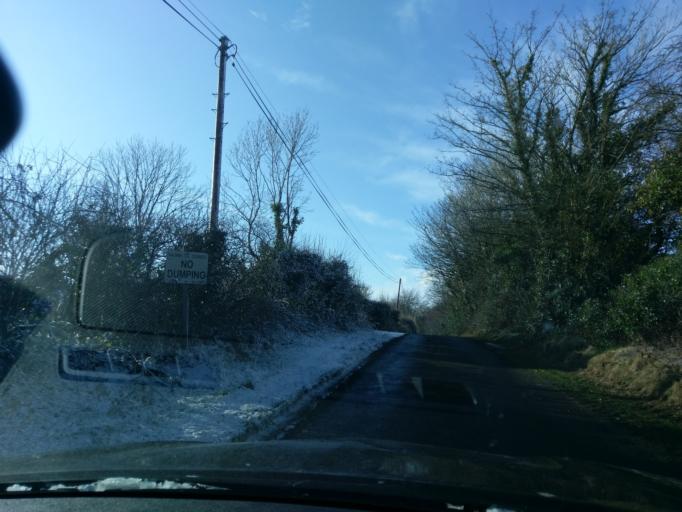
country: IE
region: Connaught
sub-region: County Galway
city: Gort
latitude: 53.1785
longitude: -8.7948
